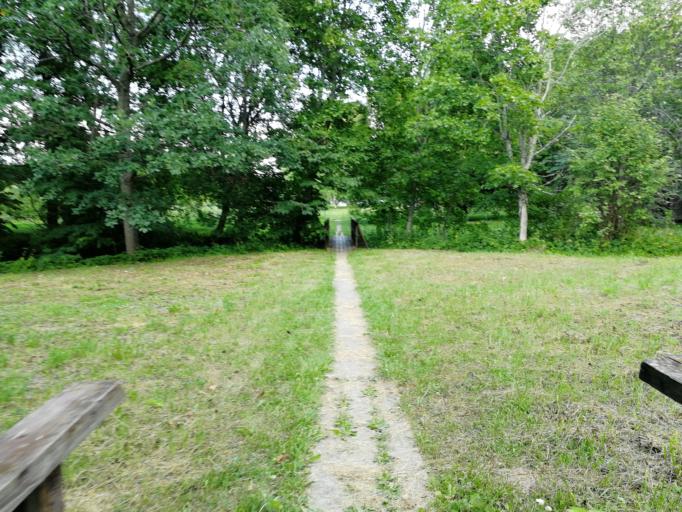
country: EE
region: Laeaene
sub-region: Lihula vald
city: Lihula
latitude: 58.7140
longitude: 23.8129
